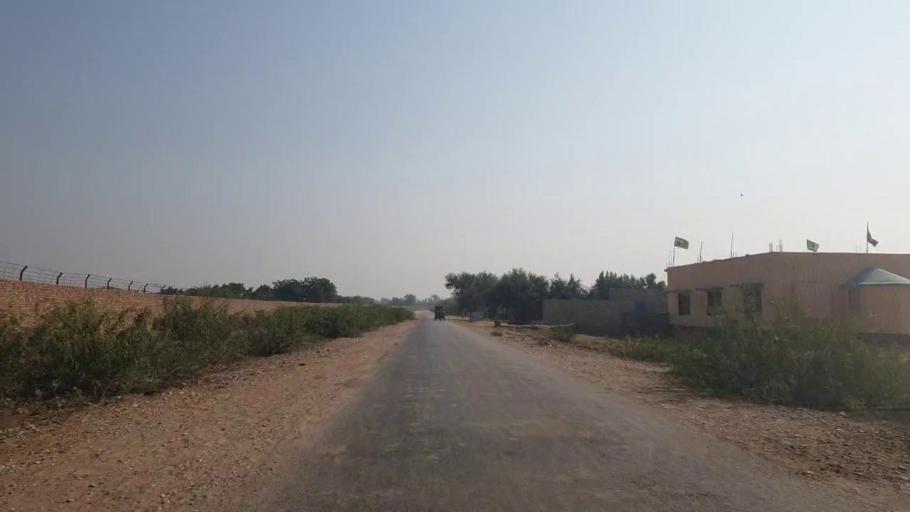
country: PK
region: Sindh
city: Jamshoro
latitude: 25.5323
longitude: 68.3241
